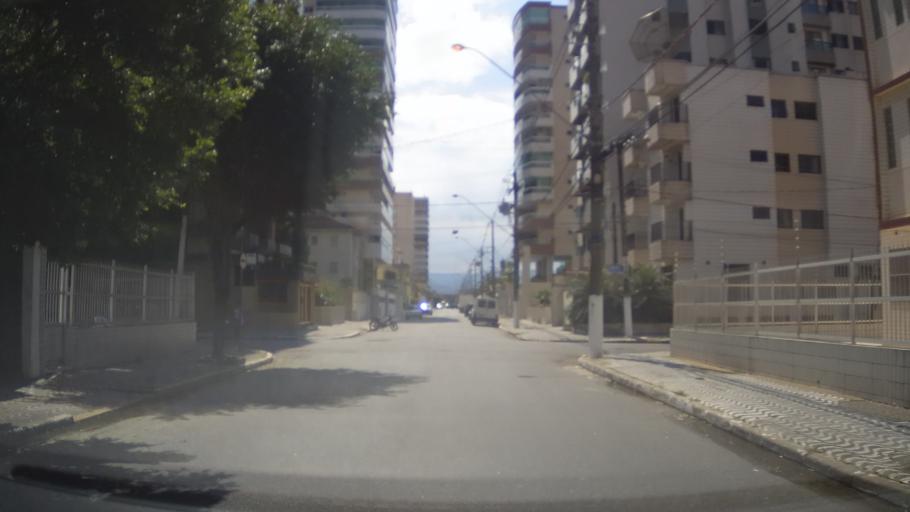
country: BR
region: Sao Paulo
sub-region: Praia Grande
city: Praia Grande
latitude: -24.0124
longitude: -46.4250
